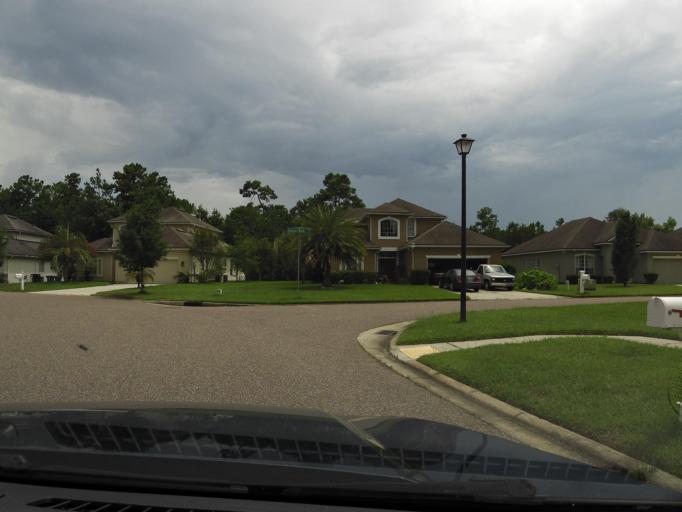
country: US
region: Florida
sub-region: Duval County
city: Jacksonville
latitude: 30.4266
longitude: -81.7186
